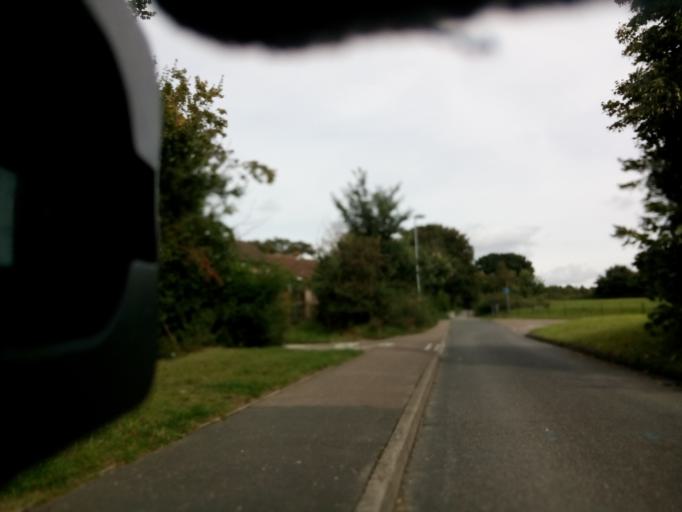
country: GB
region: England
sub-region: Norfolk
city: Bowthorpe
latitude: 52.6363
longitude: 1.2181
